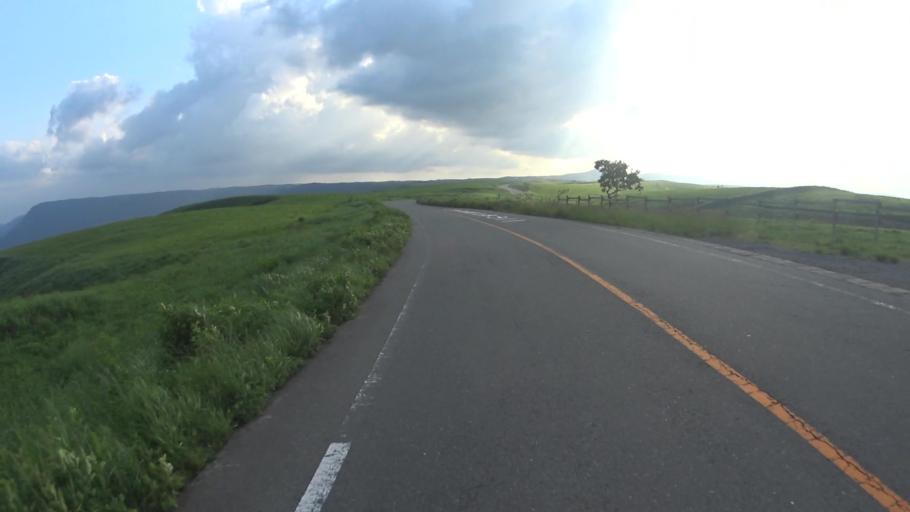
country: JP
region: Kumamoto
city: Aso
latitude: 33.0107
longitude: 131.0585
